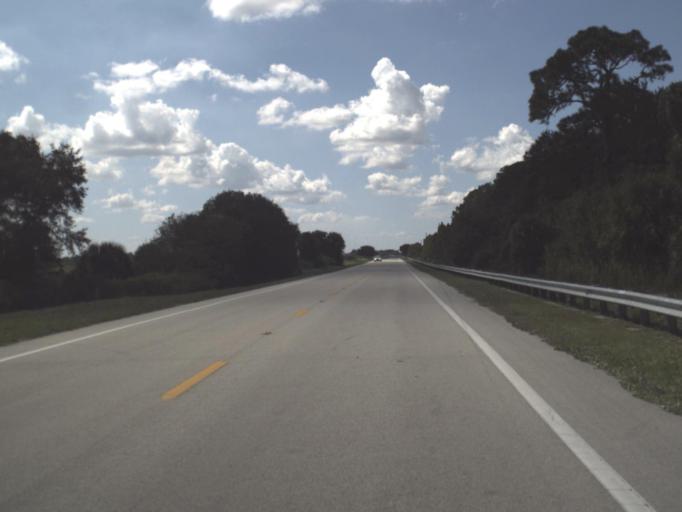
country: US
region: Florida
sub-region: Hendry County
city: Port LaBelle
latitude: 26.8125
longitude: -81.3685
